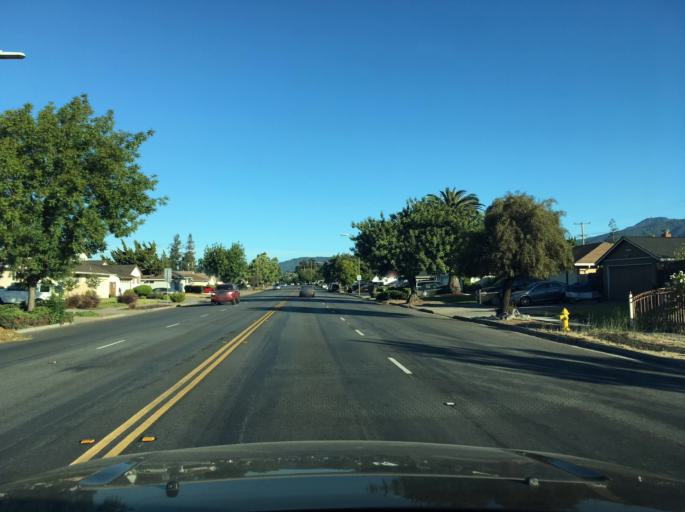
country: US
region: California
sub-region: Santa Clara County
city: Cambrian Park
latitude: 37.2486
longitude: -121.8943
